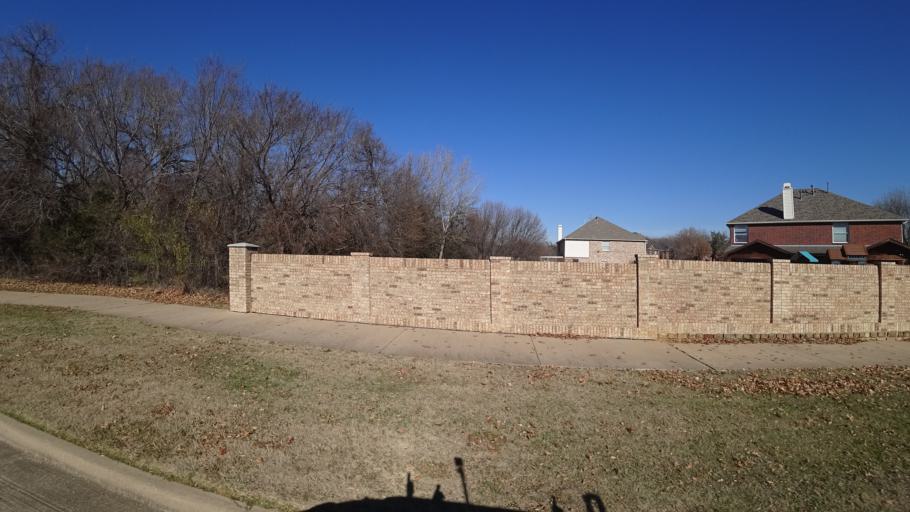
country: US
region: Texas
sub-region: Denton County
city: Lewisville
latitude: 33.0206
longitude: -97.0234
